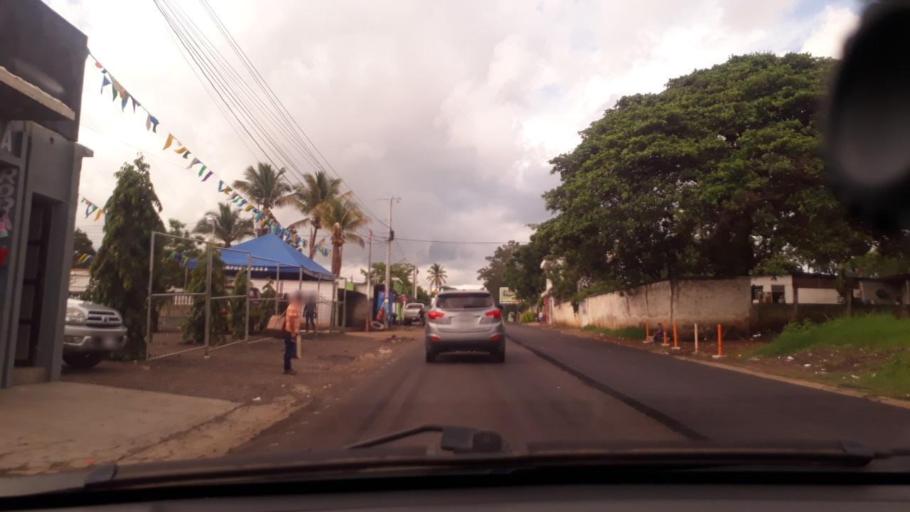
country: GT
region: Jutiapa
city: Quesada
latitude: 14.2619
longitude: -90.0199
